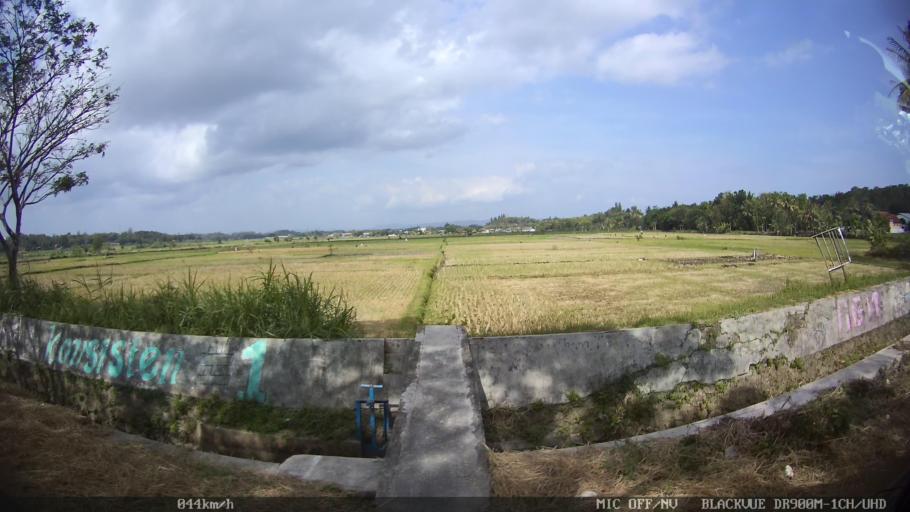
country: ID
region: Daerah Istimewa Yogyakarta
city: Kasihan
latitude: -7.8469
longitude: 110.3147
